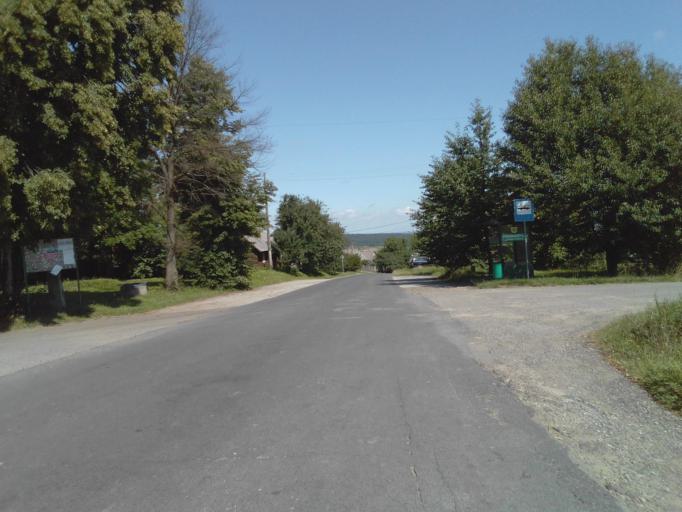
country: PL
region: Subcarpathian Voivodeship
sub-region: Powiat krosnienski
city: Jedlicze
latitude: 49.6812
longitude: 21.6147
